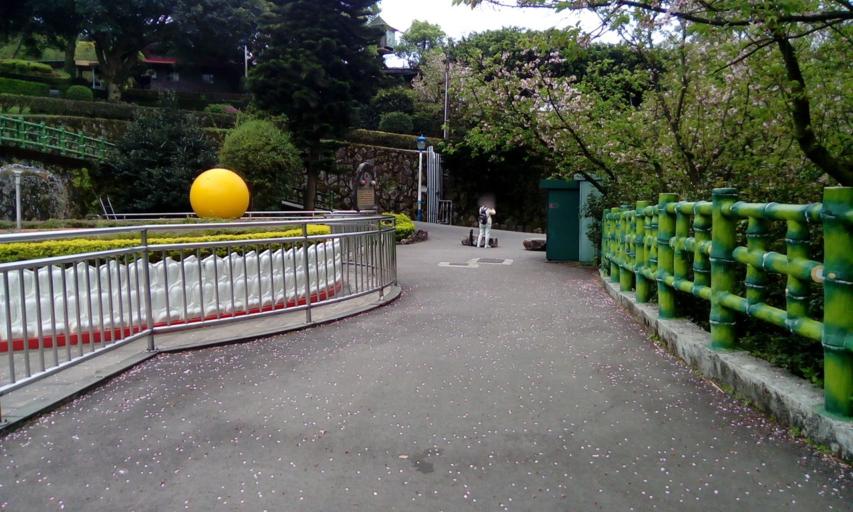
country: TW
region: Taipei
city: Taipei
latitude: 25.1856
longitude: 121.4865
